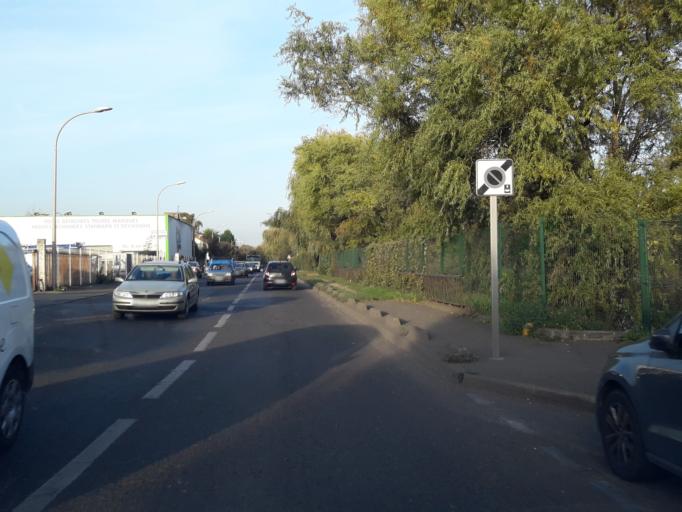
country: FR
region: Ile-de-France
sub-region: Departement de l'Essonne
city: Athis-Mons
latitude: 48.6996
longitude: 2.3968
